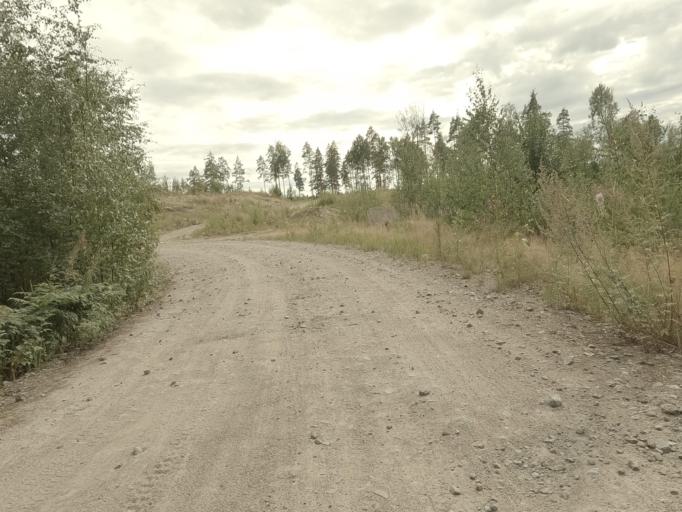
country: RU
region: Leningrad
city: Kamennogorsk
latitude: 60.9779
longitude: 29.1719
